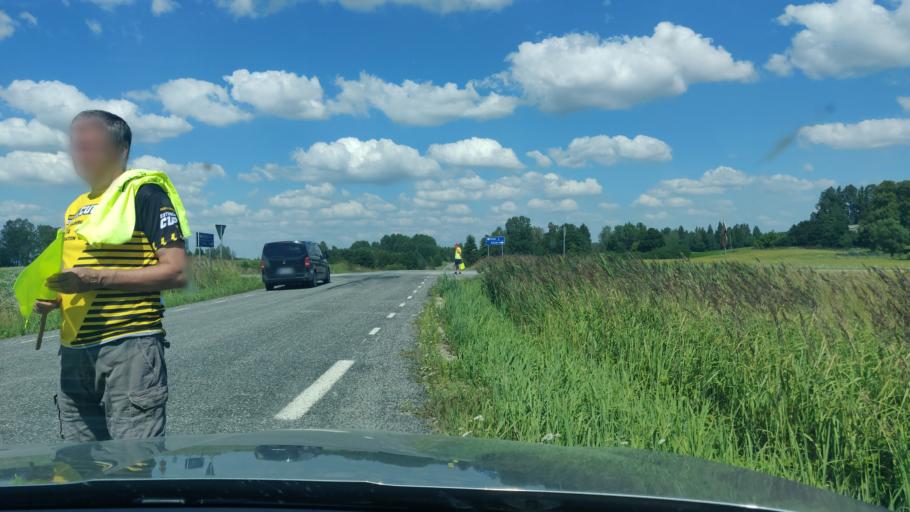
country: EE
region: Tartu
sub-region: Elva linn
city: Elva
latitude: 58.1431
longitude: 26.4764
